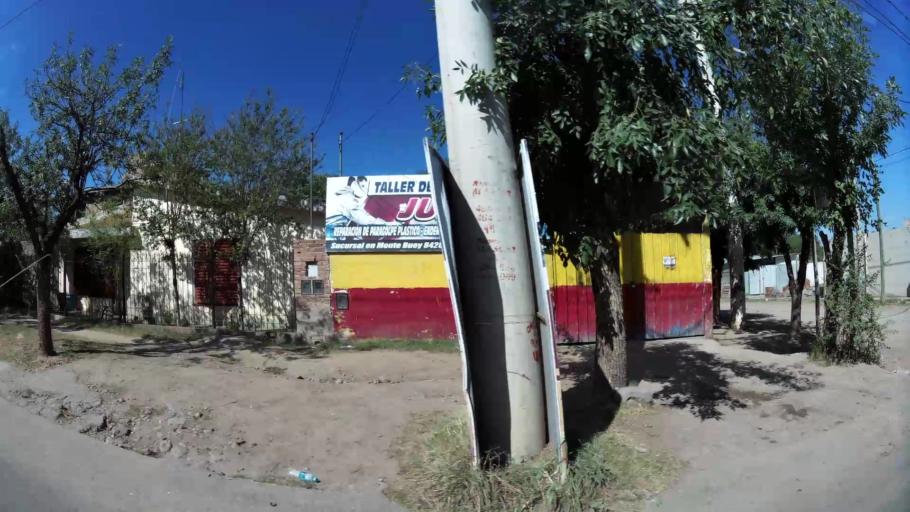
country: AR
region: Cordoba
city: Saldan
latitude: -31.3242
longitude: -64.2885
